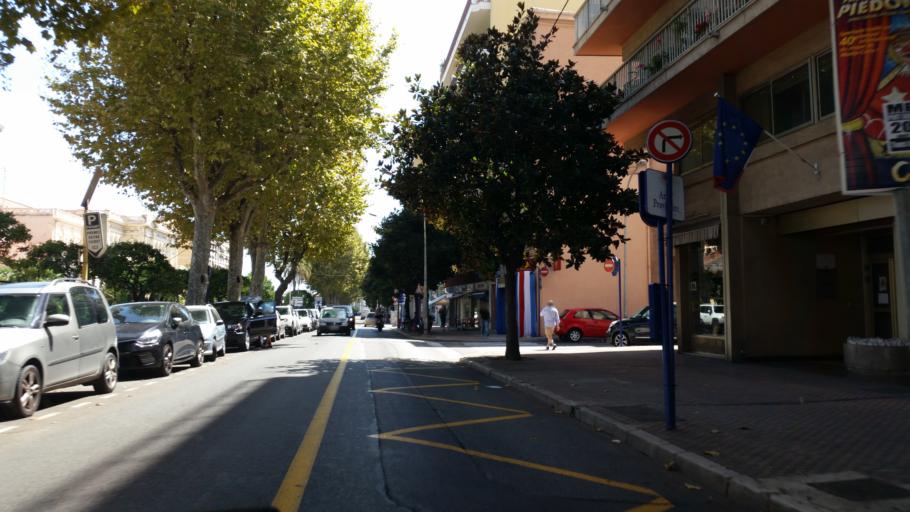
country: FR
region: Provence-Alpes-Cote d'Azur
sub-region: Departement des Alpes-Maritimes
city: Menton
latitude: 43.7750
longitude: 7.4957
